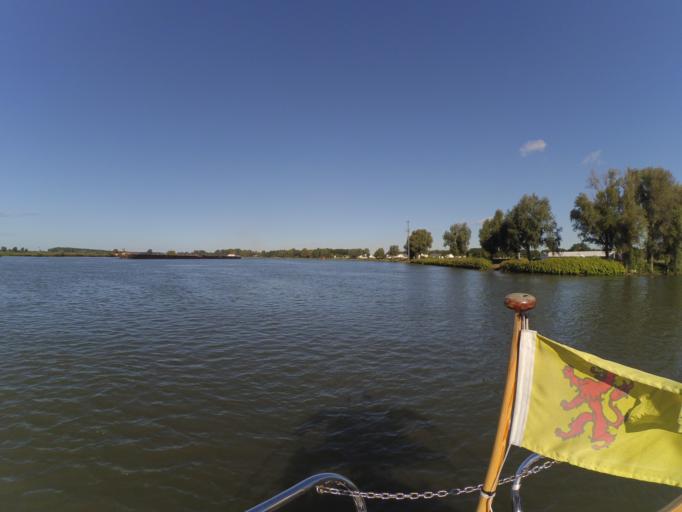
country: NL
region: South Holland
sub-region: Gemeente Zwijndrecht
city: Heerjansdam
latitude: 51.8305
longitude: 4.5541
